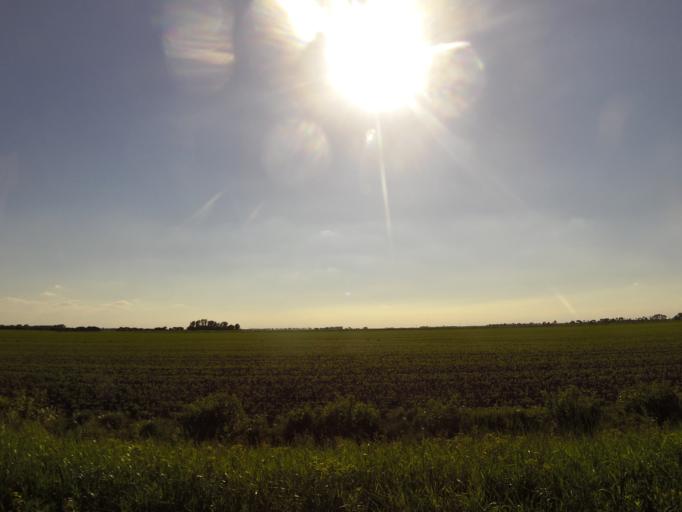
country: US
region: North Dakota
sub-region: Walsh County
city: Grafton
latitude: 48.3997
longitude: -97.2339
